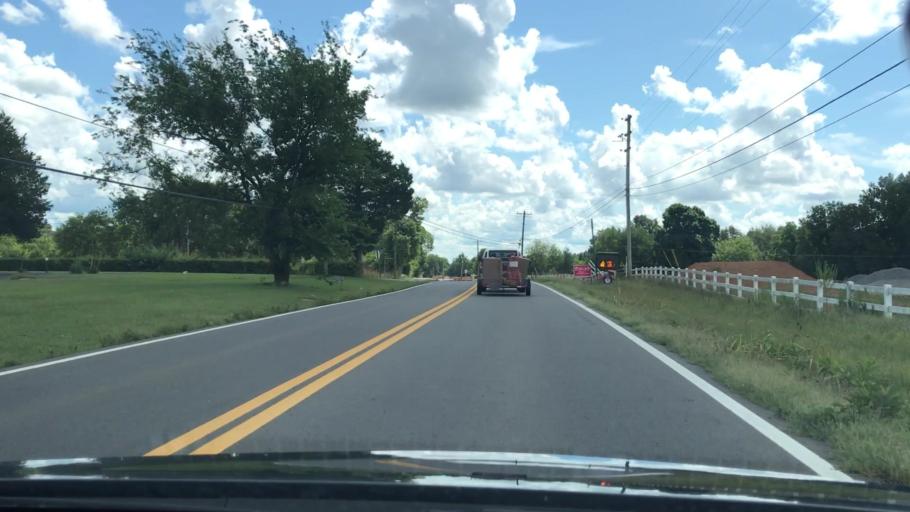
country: US
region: Tennessee
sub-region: Rutherford County
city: Smyrna
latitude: 35.8435
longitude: -86.5426
